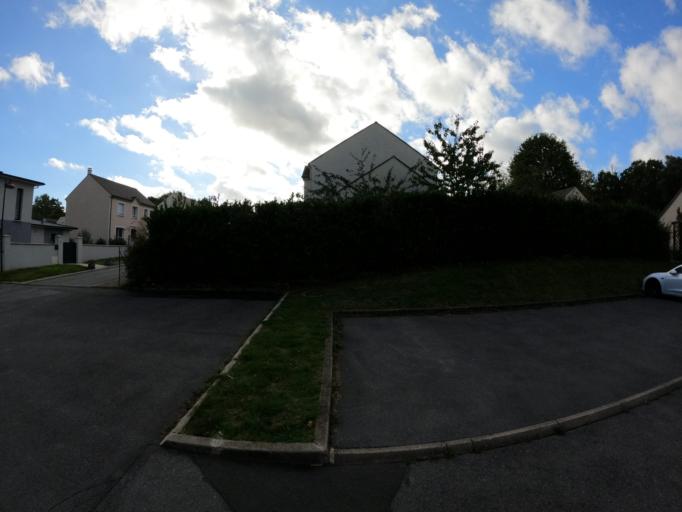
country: FR
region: Ile-de-France
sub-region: Departement de Seine-et-Marne
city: Esbly
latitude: 48.8925
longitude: 2.8172
